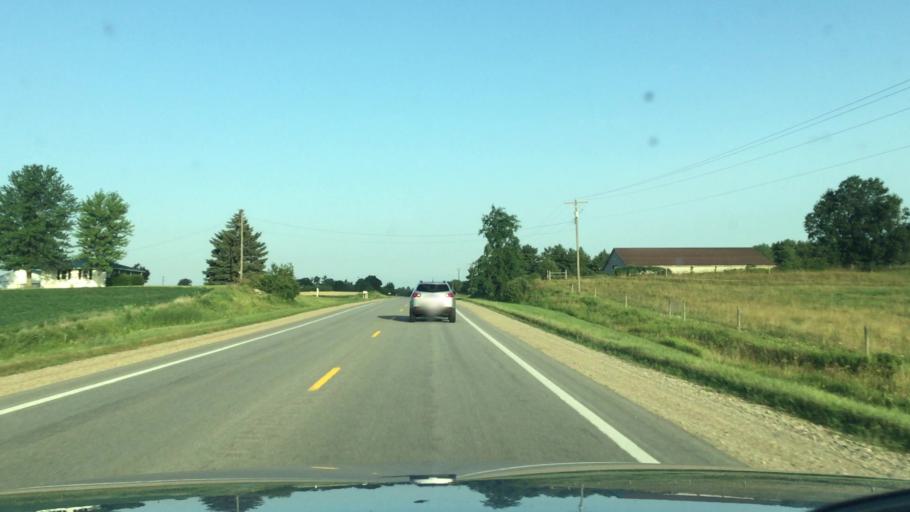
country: US
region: Michigan
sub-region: Gratiot County
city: Ithaca
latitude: 43.1760
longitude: -84.6231
